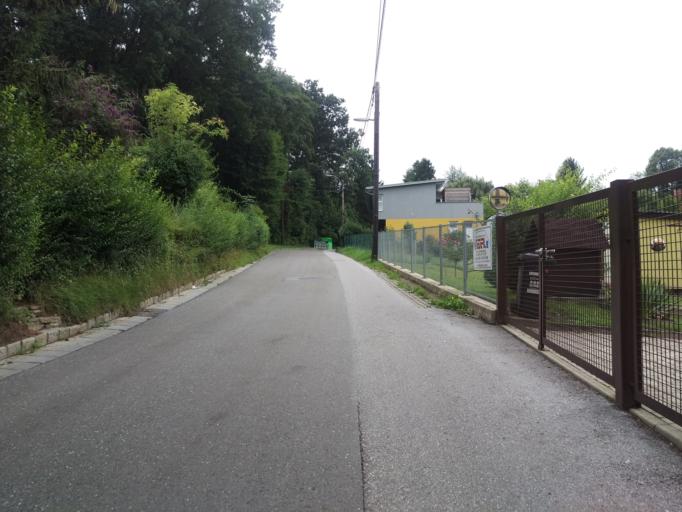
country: AT
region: Styria
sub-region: Politischer Bezirk Graz-Umgebung
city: Raaba
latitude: 47.0558
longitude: 15.4817
